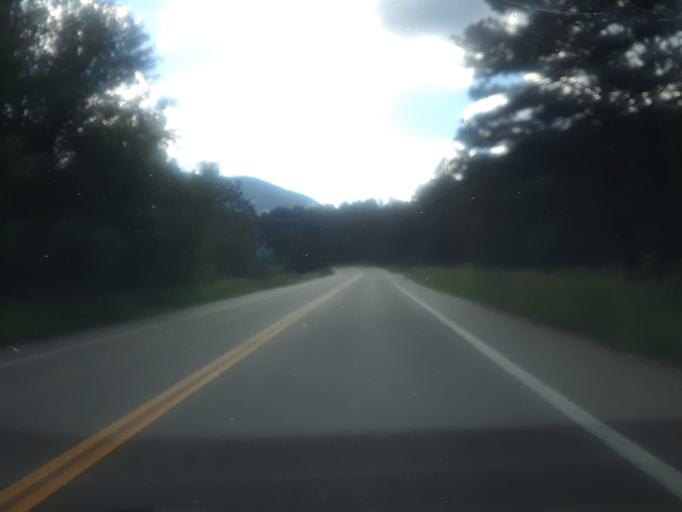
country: US
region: Colorado
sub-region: Jefferson County
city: Kittredge
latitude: 39.7170
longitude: -105.3860
